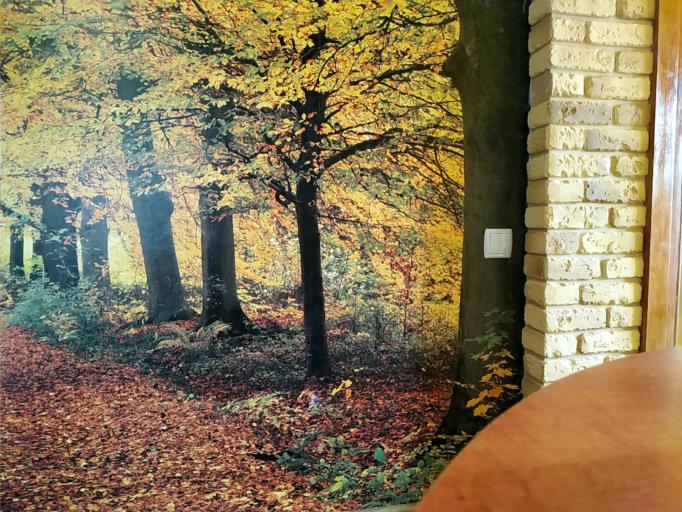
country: RU
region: Leningrad
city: Volosovo
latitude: 59.0300
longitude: 29.2899
